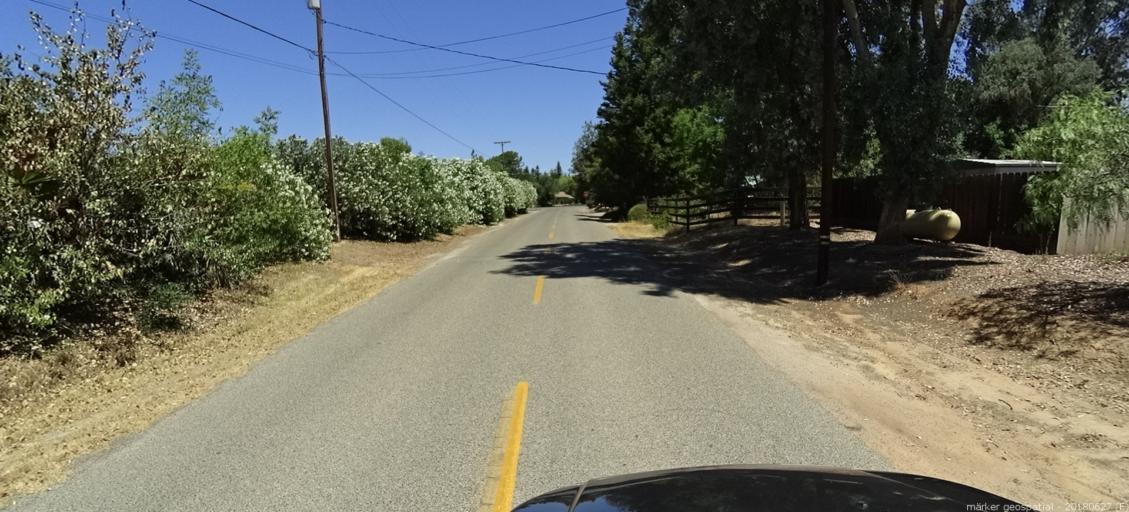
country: US
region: California
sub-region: Madera County
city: Bonadelle Ranchos-Madera Ranchos
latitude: 36.9273
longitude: -119.8692
